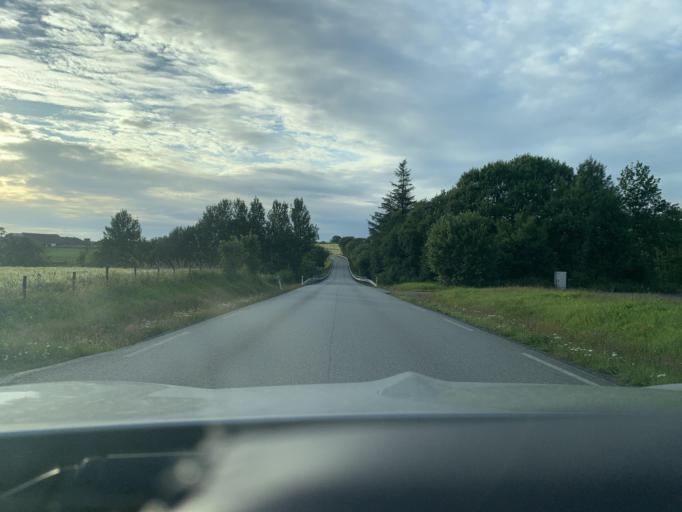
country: NO
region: Rogaland
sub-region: Time
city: Bryne
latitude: 58.7048
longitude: 5.6961
